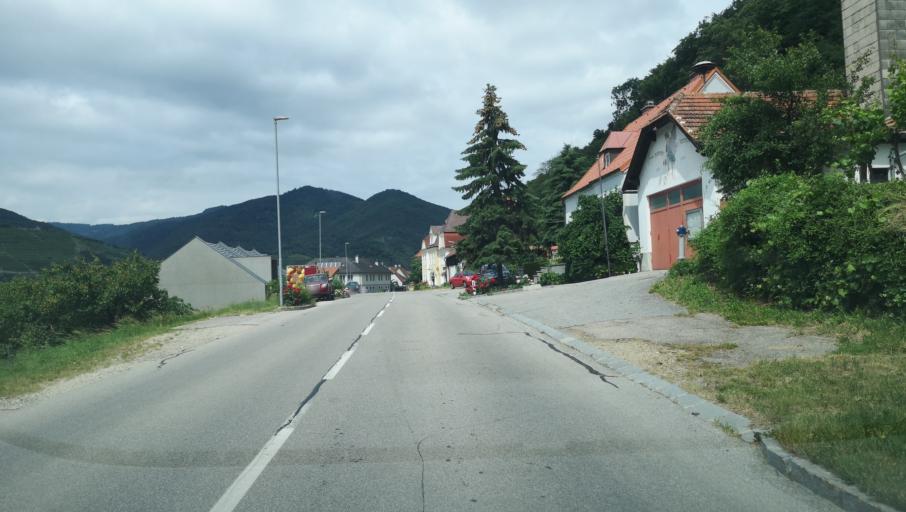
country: AT
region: Lower Austria
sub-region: Politischer Bezirk Krems
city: Spitz
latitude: 48.3519
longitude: 15.4135
